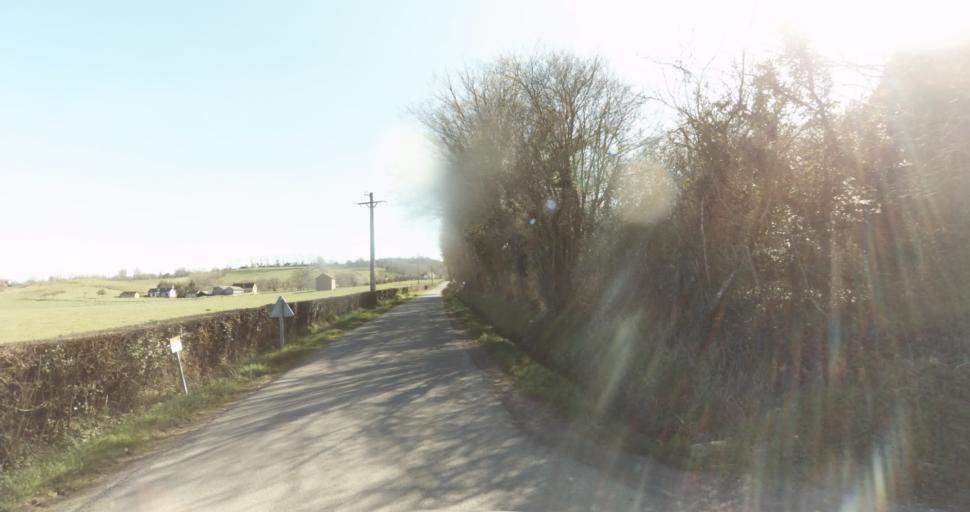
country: FR
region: Lower Normandy
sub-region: Departement du Calvados
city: Saint-Pierre-sur-Dives
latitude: 49.0265
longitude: 0.0560
